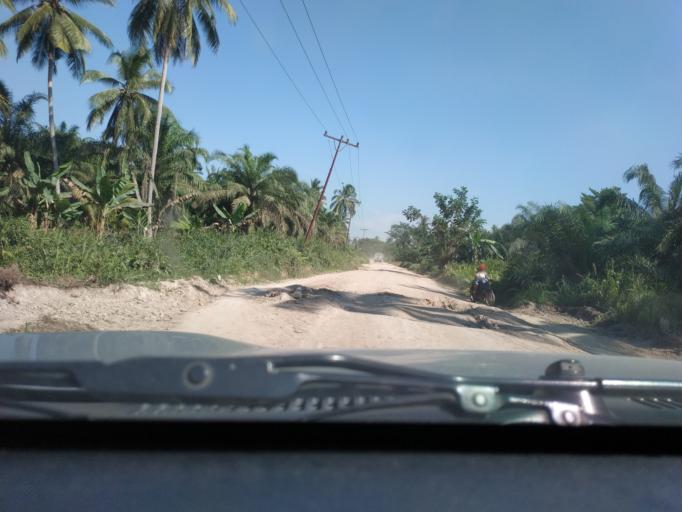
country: ID
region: North Sumatra
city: Tanjungbalai
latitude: 2.8419
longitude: 99.9533
